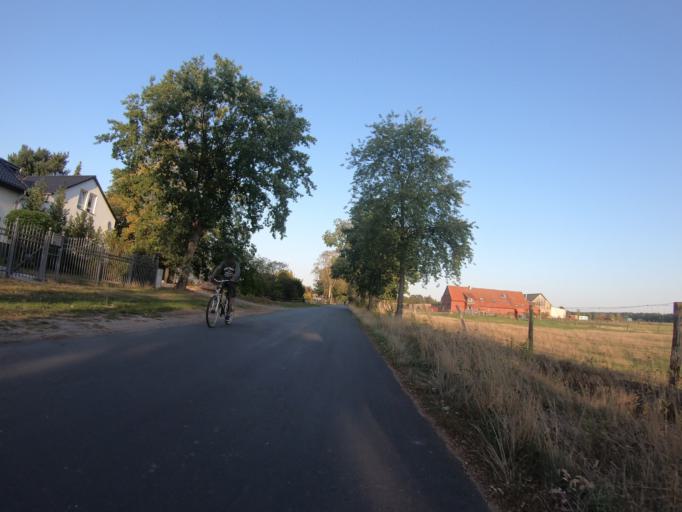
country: DE
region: Lower Saxony
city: Gifhorn
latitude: 52.4682
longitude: 10.5835
